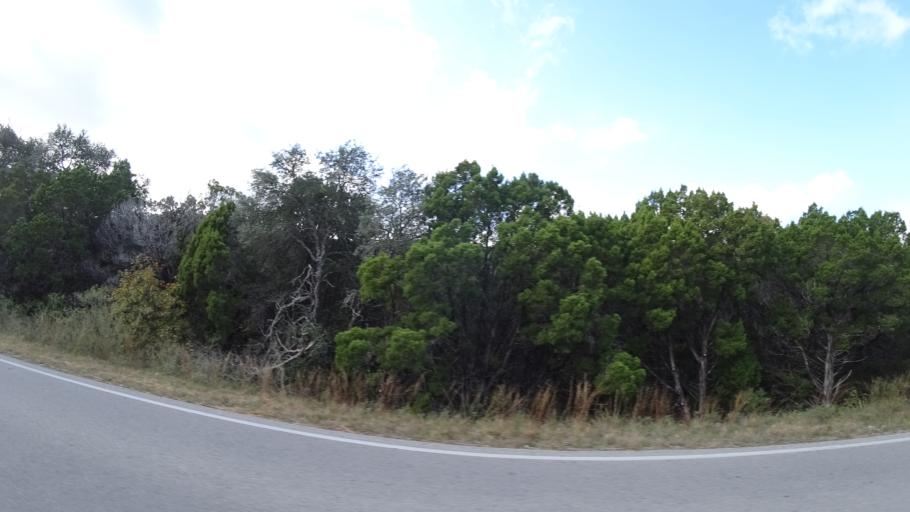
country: US
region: Texas
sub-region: Travis County
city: Hudson Bend
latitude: 30.4239
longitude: -97.8719
